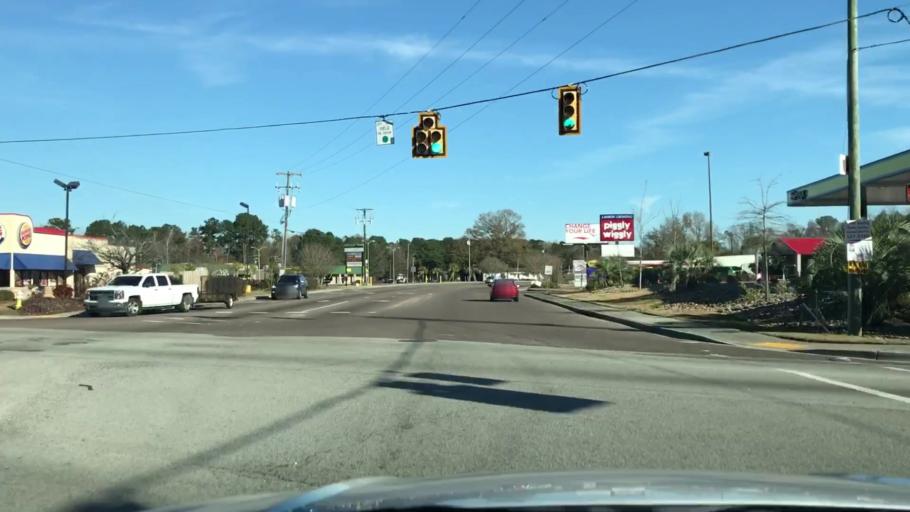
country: US
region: South Carolina
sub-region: Berkeley County
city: Ladson
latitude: 32.9897
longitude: -80.1008
